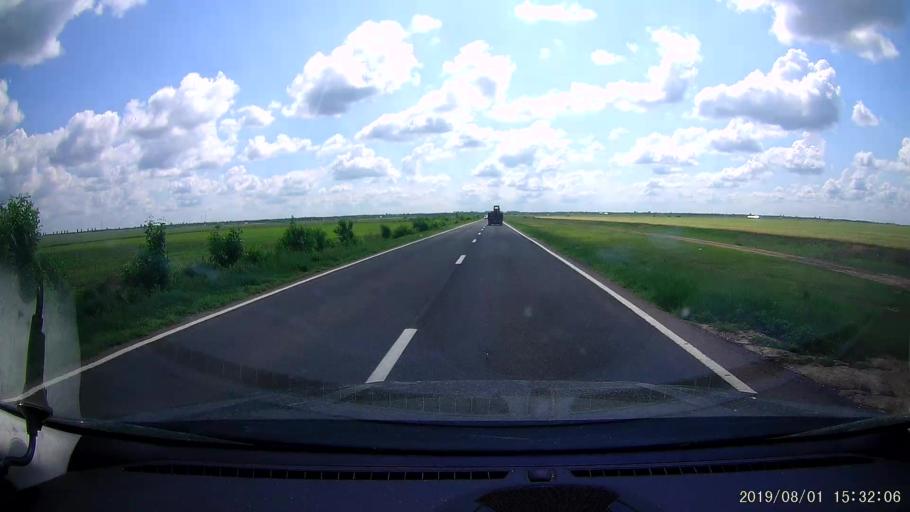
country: RO
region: Braila
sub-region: Comuna Insuratei
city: Insuratei
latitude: 44.9360
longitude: 27.6443
